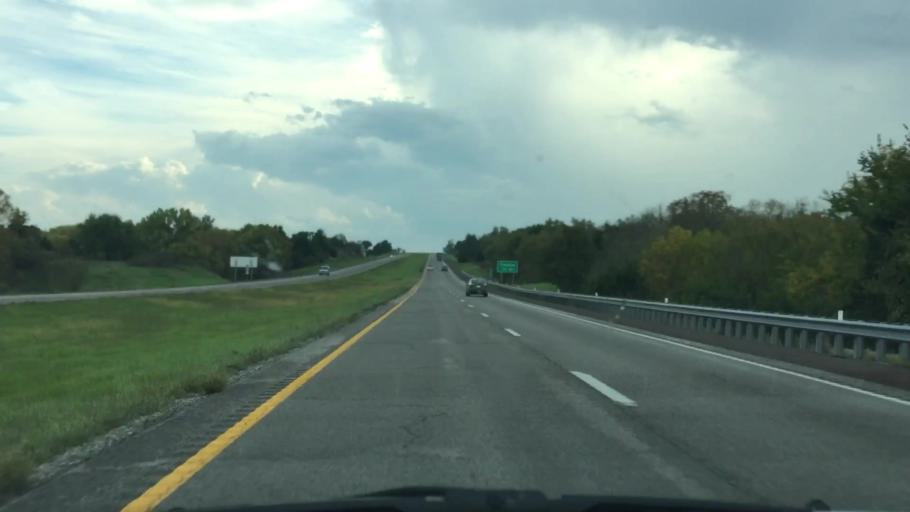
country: US
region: Missouri
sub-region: Clinton County
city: Cameron
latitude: 39.8673
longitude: -94.1708
